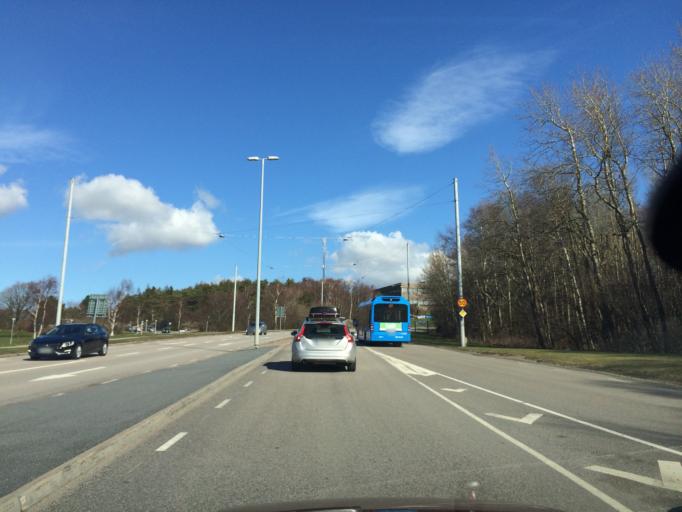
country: SE
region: Vaestra Goetaland
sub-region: Goteborg
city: Majorna
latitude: 57.7238
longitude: 11.8511
